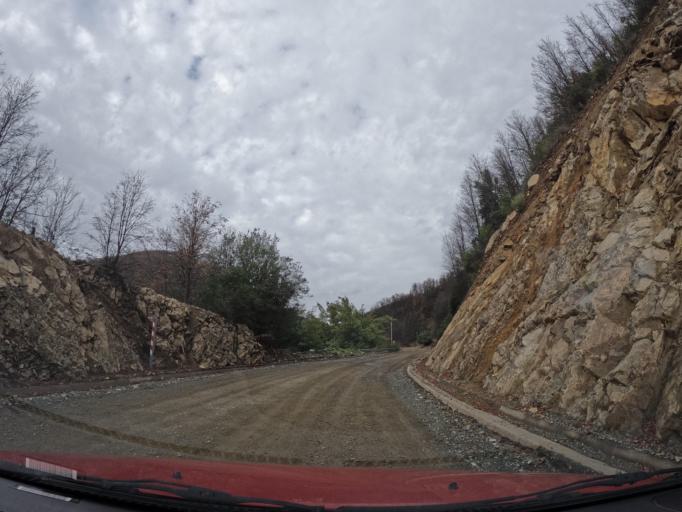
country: CL
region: Maule
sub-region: Provincia de Linares
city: Colbun
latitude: -35.8575
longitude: -71.1897
